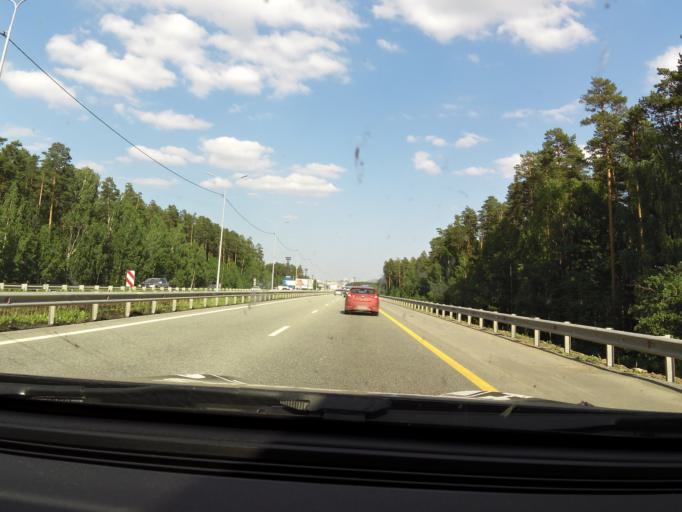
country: RU
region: Sverdlovsk
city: Shirokaya Rechka
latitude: 56.8253
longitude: 60.4741
